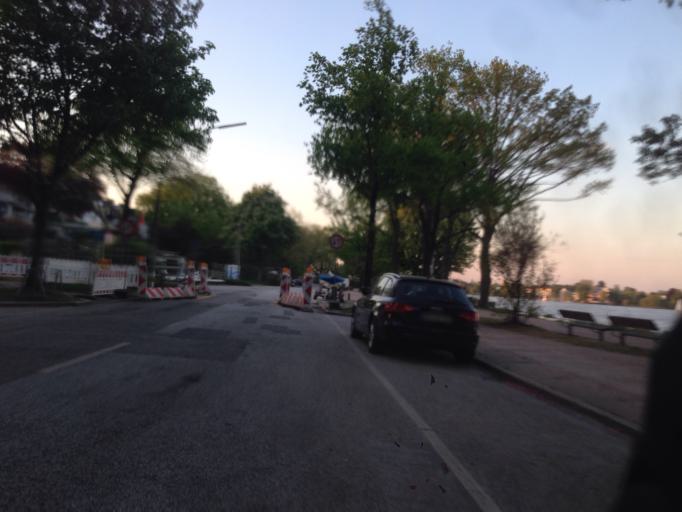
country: DE
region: Hamburg
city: Altstadt
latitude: 53.5651
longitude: 9.9997
